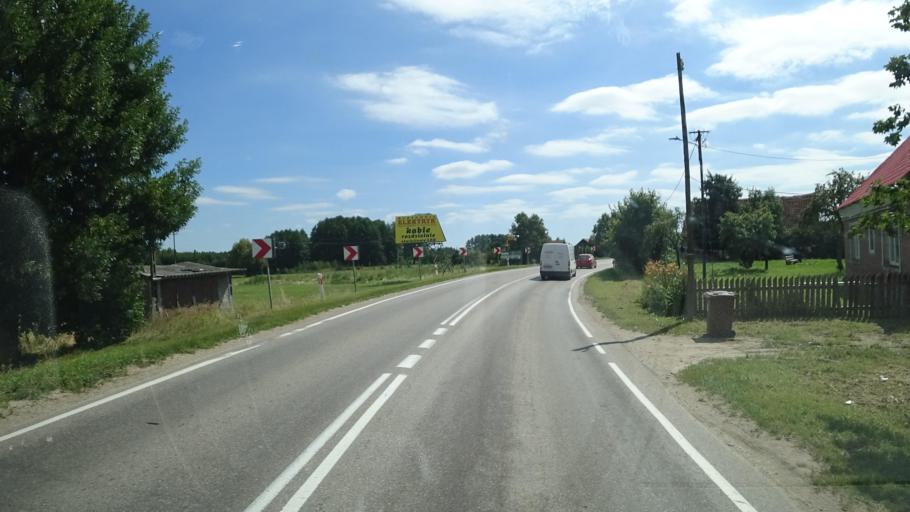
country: PL
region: Warmian-Masurian Voivodeship
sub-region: Powiat elcki
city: Elk
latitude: 53.7486
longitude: 22.3447
